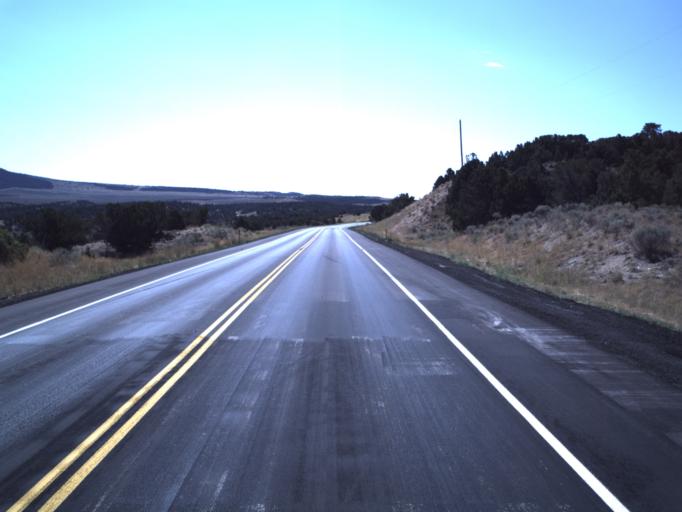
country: US
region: Utah
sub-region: Utah County
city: Eagle Mountain
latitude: 40.0331
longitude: -112.2854
